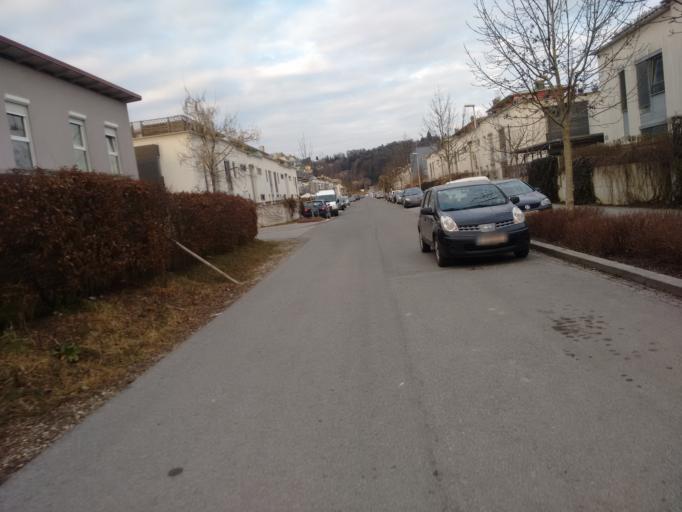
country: AT
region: Styria
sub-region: Politischer Bezirk Graz-Umgebung
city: Raaba
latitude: 47.0441
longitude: 15.4728
